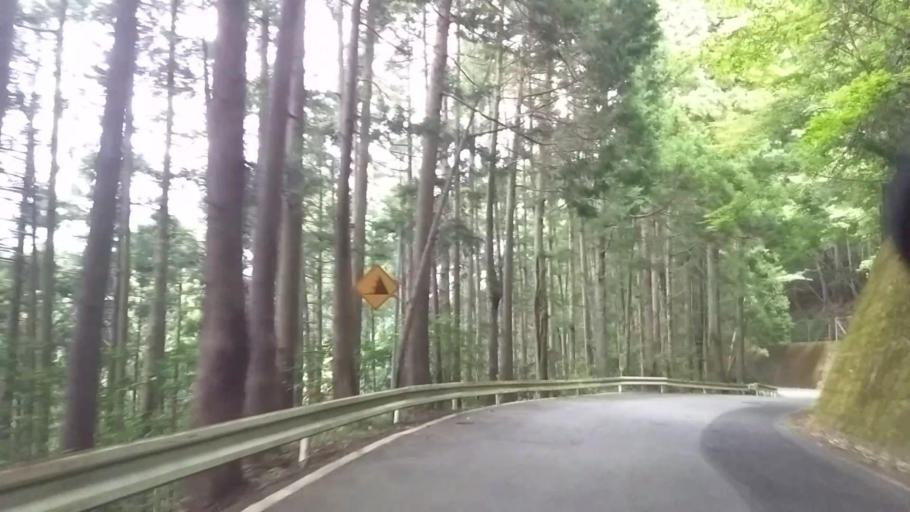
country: JP
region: Shizuoka
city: Fujinomiya
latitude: 35.2196
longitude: 138.5322
